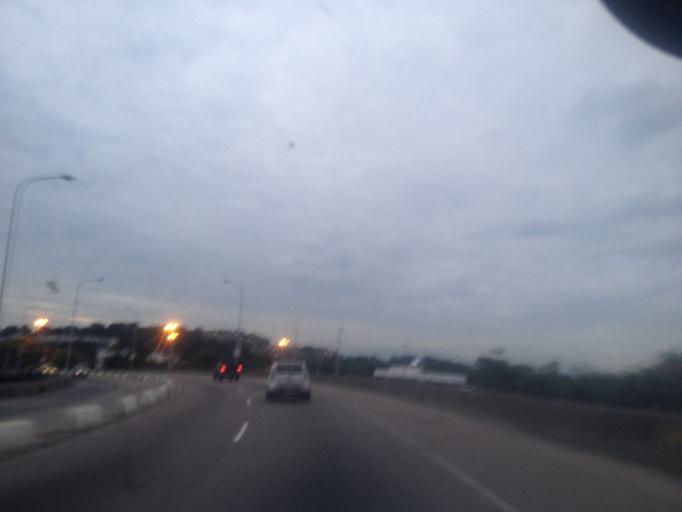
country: BR
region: Rio de Janeiro
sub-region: Rio De Janeiro
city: Rio de Janeiro
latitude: -22.8242
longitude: -43.2309
